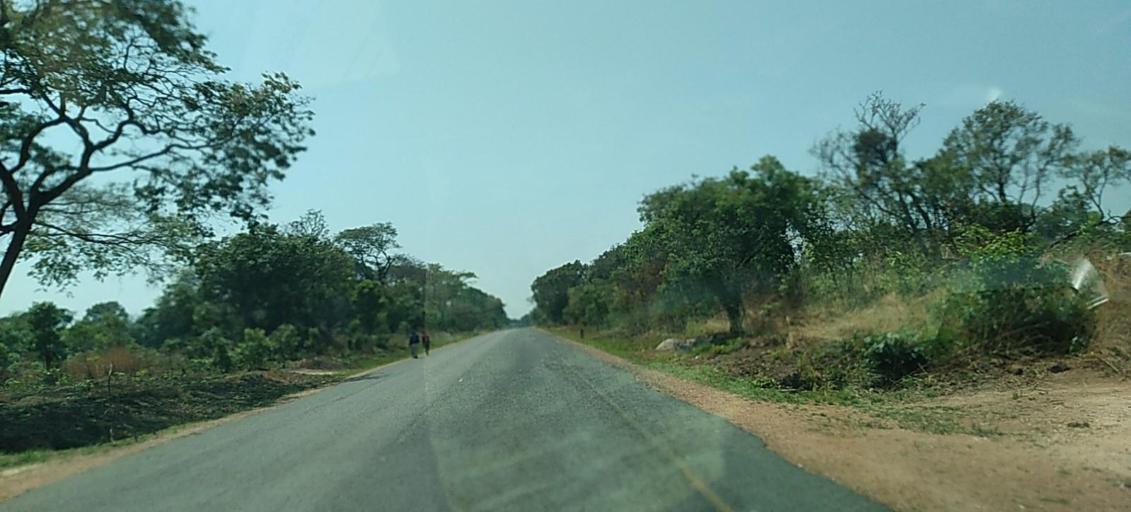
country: ZM
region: North-Western
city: Solwezi
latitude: -12.2945
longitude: 25.8197
